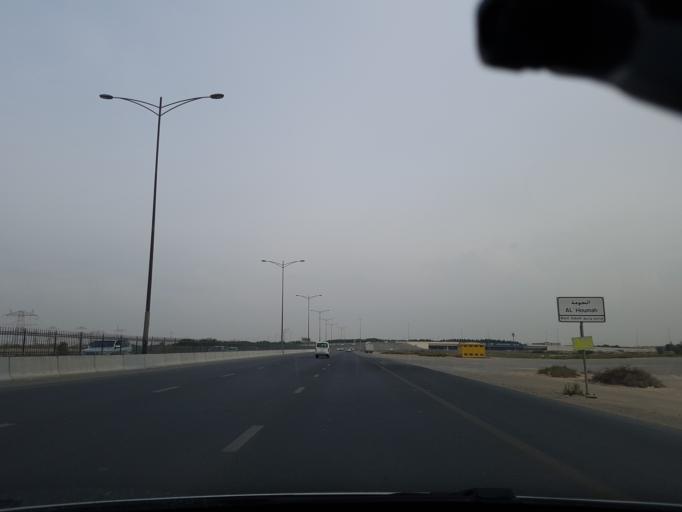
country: AE
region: Ajman
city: Ajman
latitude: 25.3615
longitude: 55.4770
